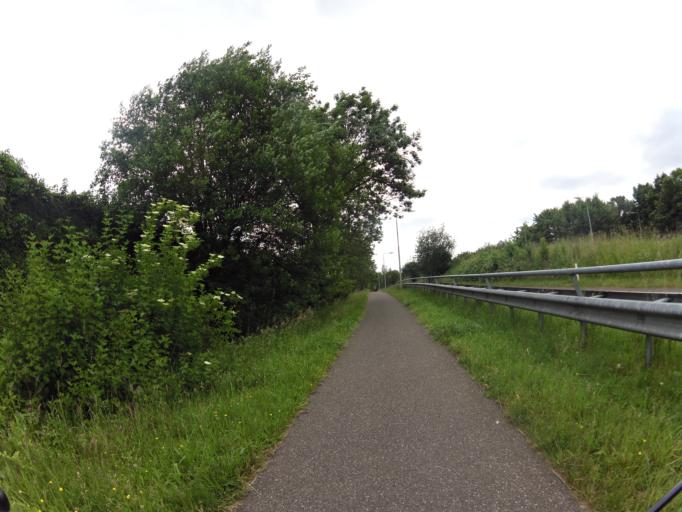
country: NL
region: Limburg
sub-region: Gemeente Kerkrade
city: Kerkrade
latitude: 50.8821
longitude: 6.0596
